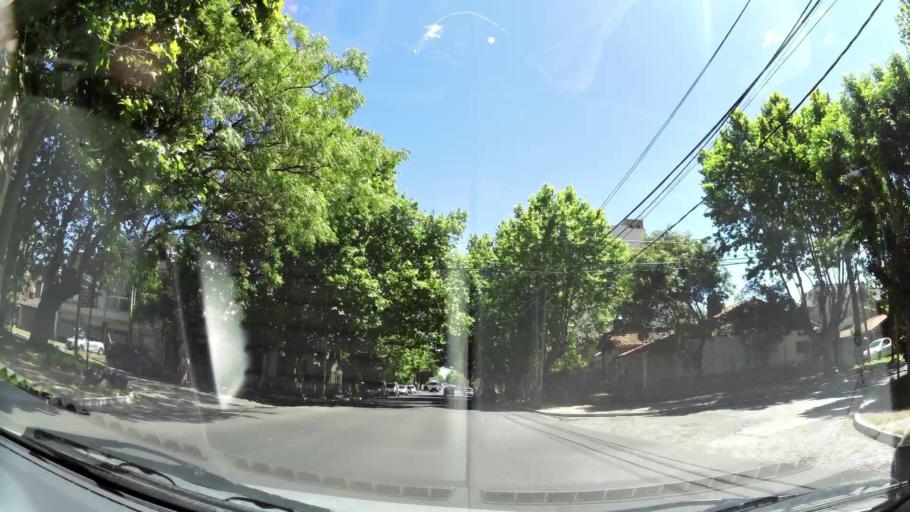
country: AR
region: Buenos Aires
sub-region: Partido de Quilmes
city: Quilmes
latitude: -34.7210
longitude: -58.2673
